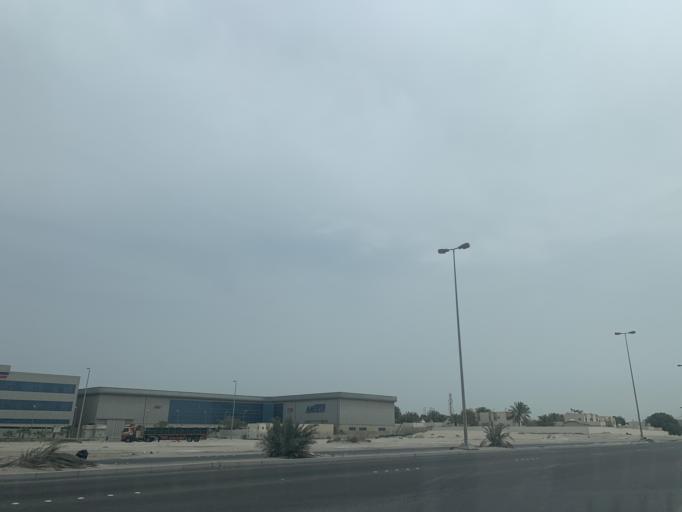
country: BH
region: Muharraq
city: Al Hadd
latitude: 26.2142
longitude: 50.6578
